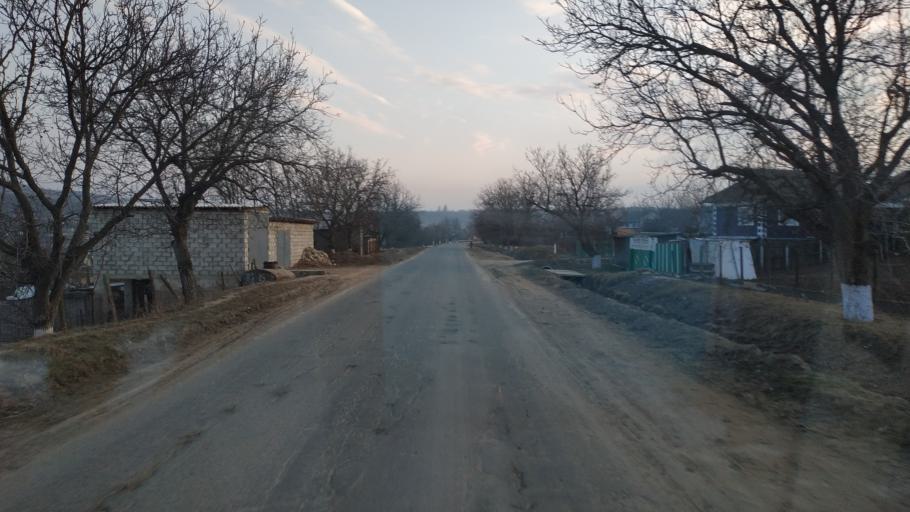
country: MD
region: Hincesti
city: Dancu
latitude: 46.6768
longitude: 28.3350
